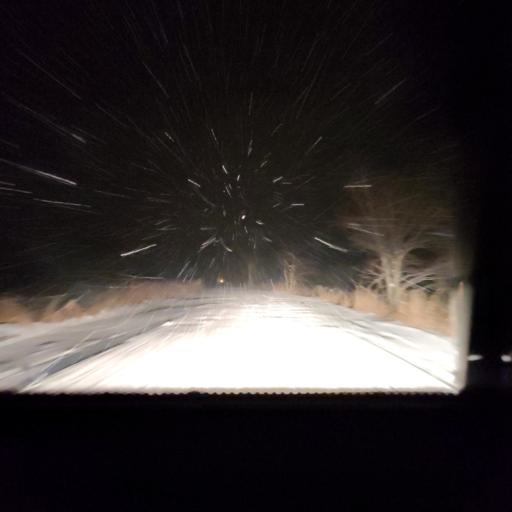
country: RU
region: Bashkortostan
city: Iglino
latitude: 54.9046
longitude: 56.2944
